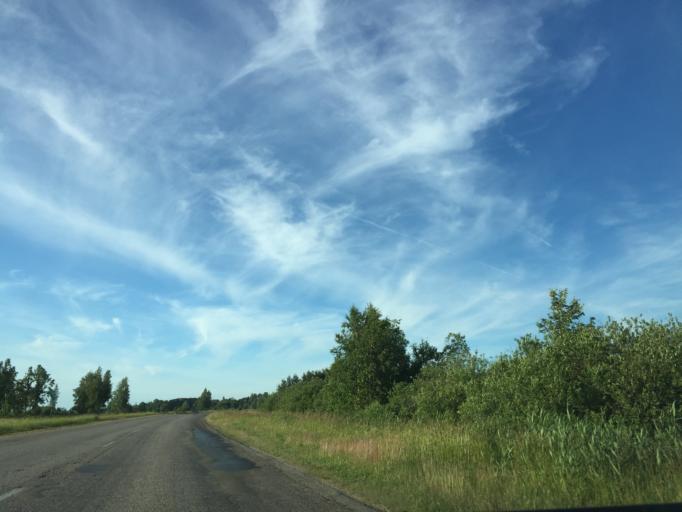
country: LV
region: Ventspils
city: Ventspils
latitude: 57.3345
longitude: 21.5641
